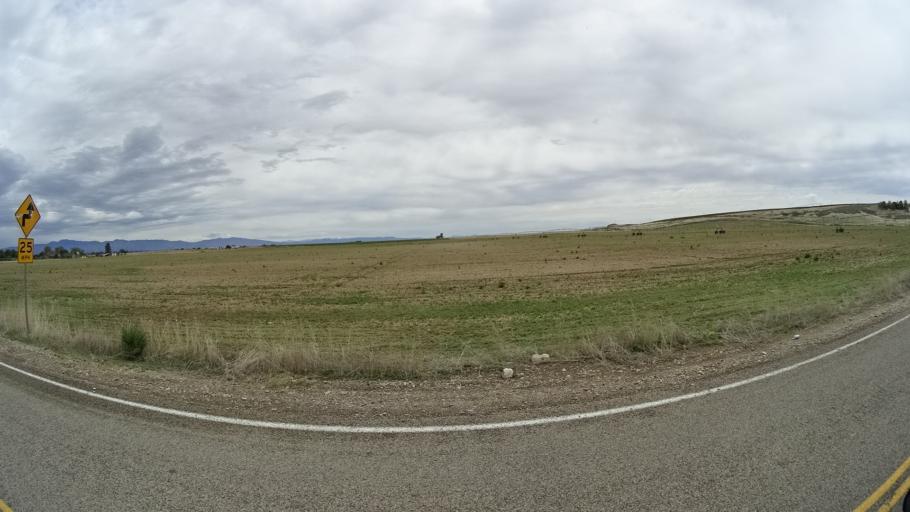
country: US
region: Idaho
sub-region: Ada County
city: Kuna
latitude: 43.4669
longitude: -116.4434
